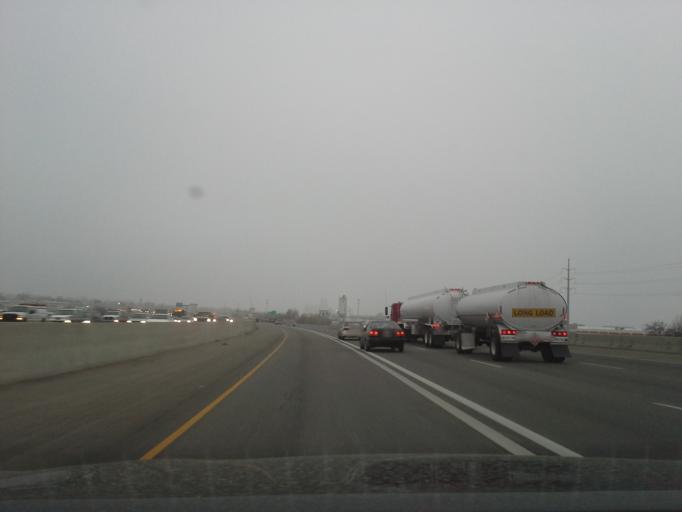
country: US
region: Utah
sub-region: Davis County
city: Kaysville
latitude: 41.0451
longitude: -111.9565
